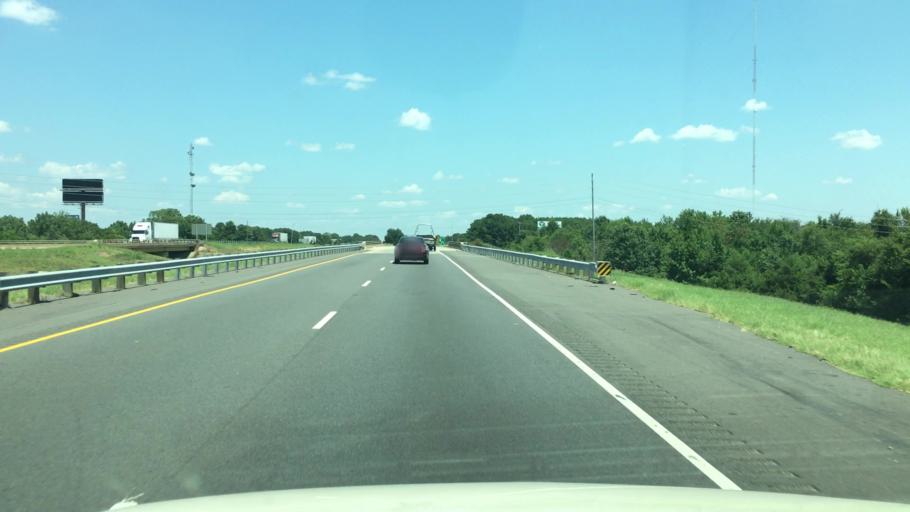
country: US
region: Arkansas
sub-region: Hempstead County
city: Hope
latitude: 33.6883
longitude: -93.6015
